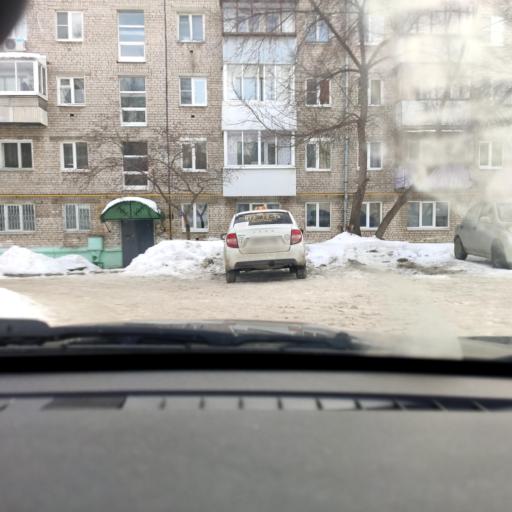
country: RU
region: Samara
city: Pribrezhnyy
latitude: 53.4866
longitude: 49.8474
